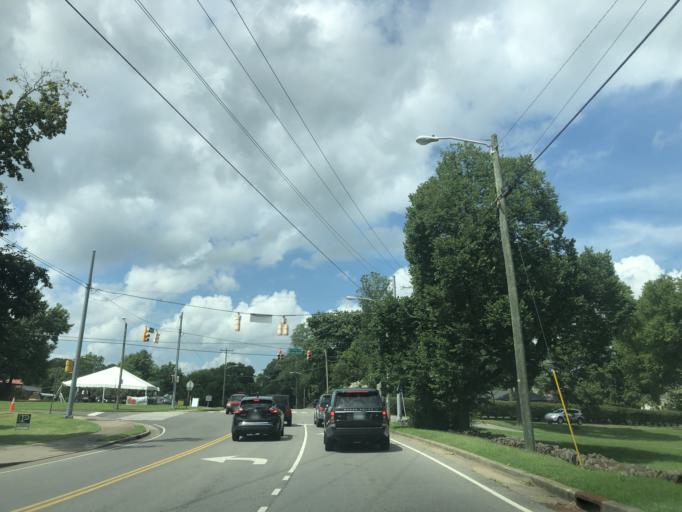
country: US
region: Tennessee
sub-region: Davidson County
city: Oak Hill
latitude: 36.0942
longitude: -86.8013
